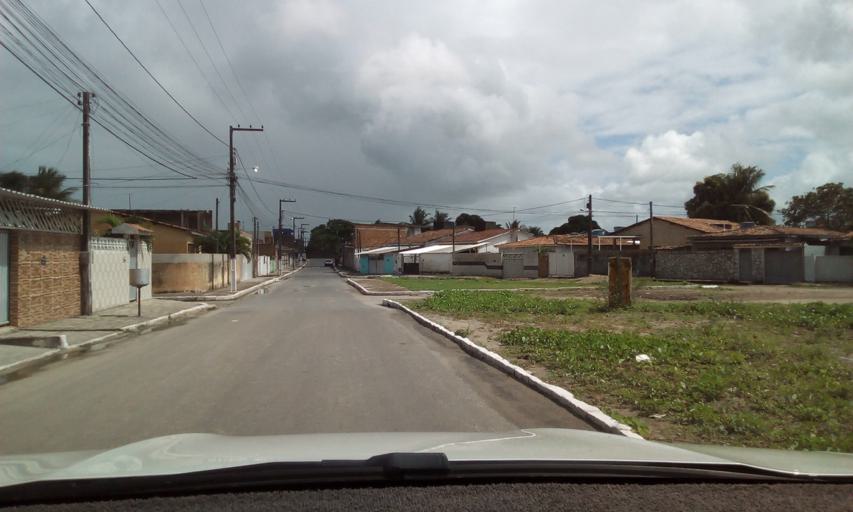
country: BR
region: Paraiba
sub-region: Santa Rita
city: Santa Rita
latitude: -7.1427
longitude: -34.9661
